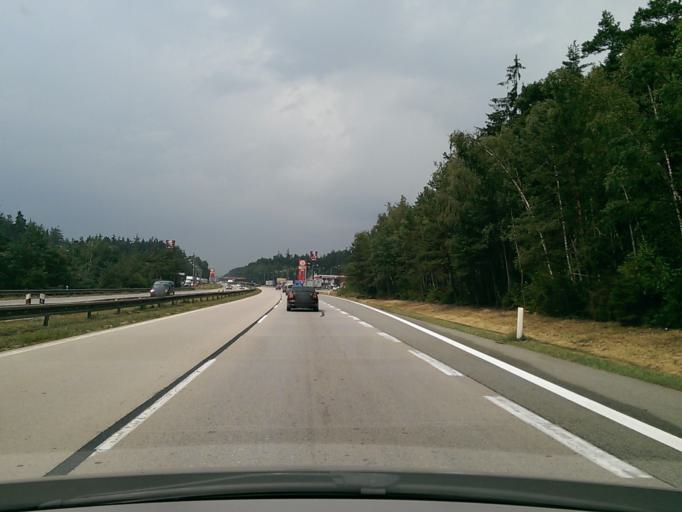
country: CZ
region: South Moravian
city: Zbraslav
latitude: 49.2695
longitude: 16.2835
